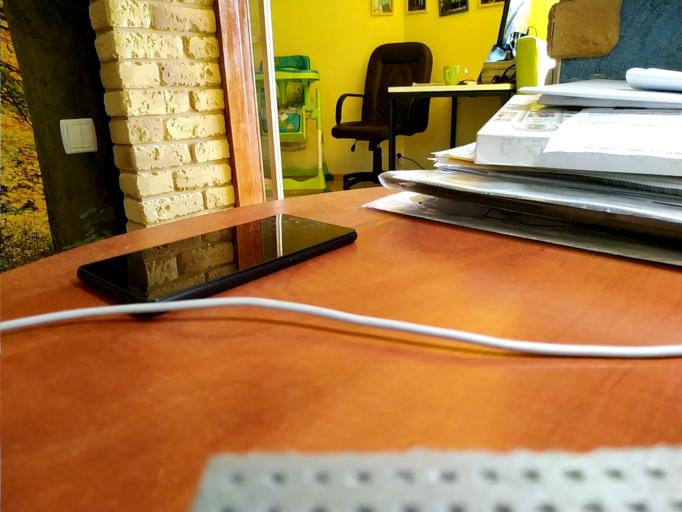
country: RU
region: Tverskaya
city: Kalashnikovo
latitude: 57.3777
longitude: 35.3699
